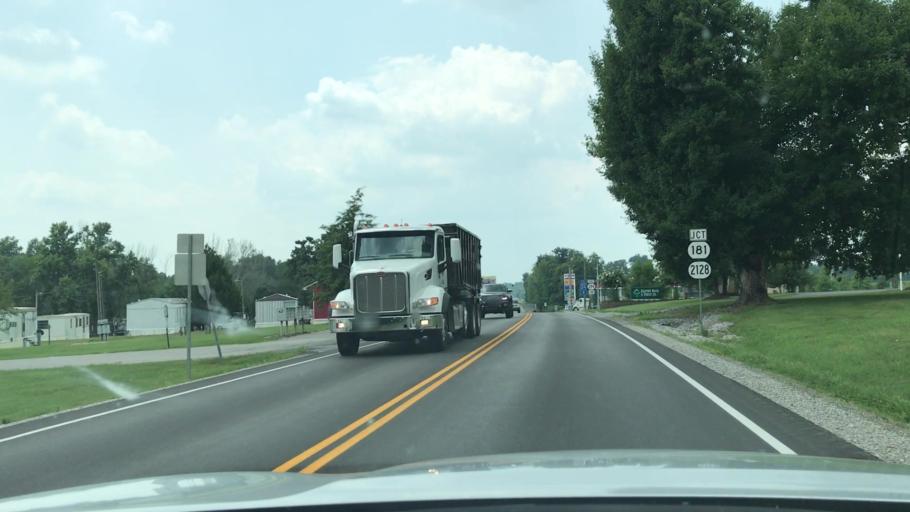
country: US
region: Kentucky
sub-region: Todd County
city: Guthrie
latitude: 36.6457
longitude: -87.1986
